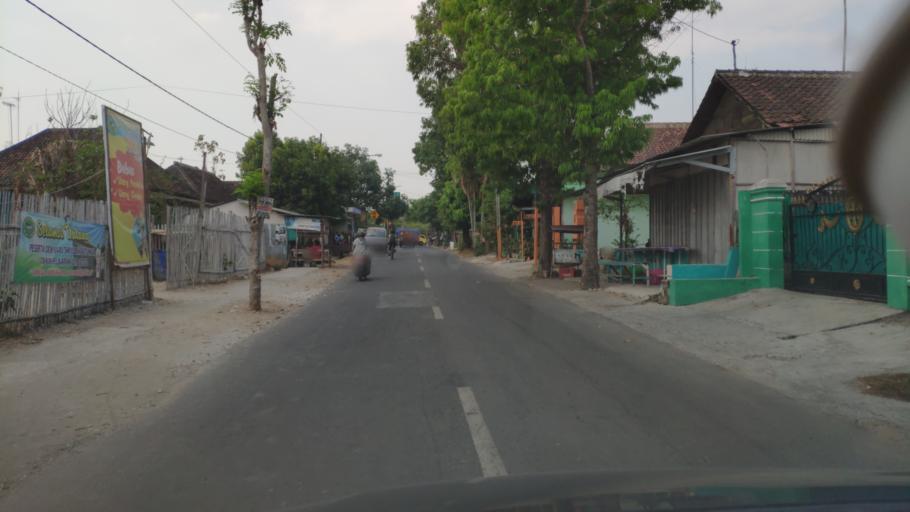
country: ID
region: Central Java
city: Kunden
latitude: -6.9595
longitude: 111.4136
